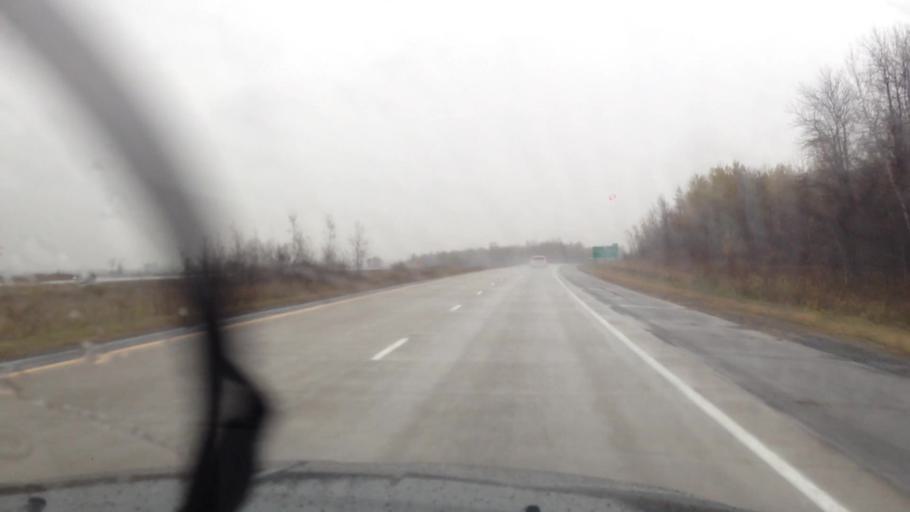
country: CA
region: Ontario
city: Hawkesbury
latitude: 45.4249
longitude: -74.7602
